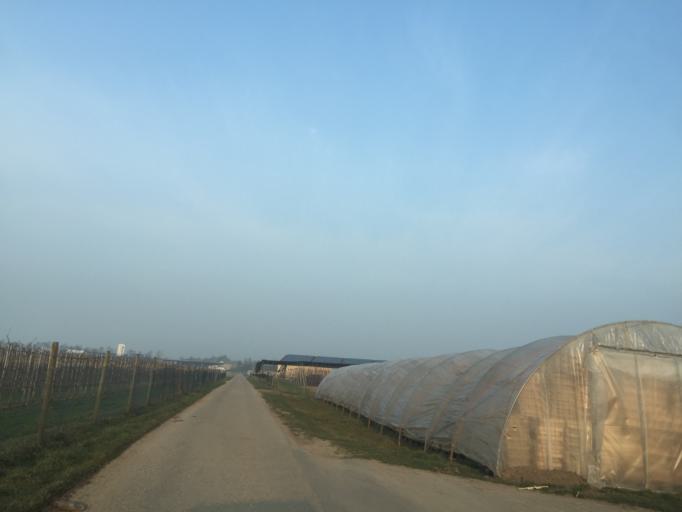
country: DE
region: Baden-Wuerttemberg
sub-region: Karlsruhe Region
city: Weinheim
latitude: 49.5146
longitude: 8.6474
